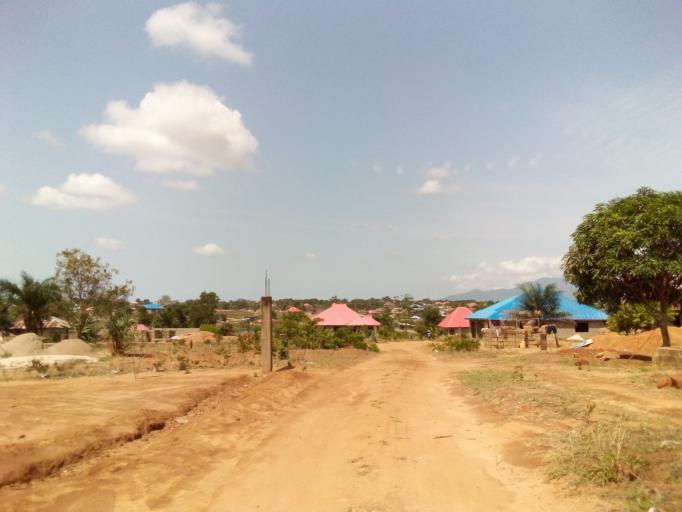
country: SL
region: Western Area
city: Waterloo
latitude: 8.3440
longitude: -13.0194
